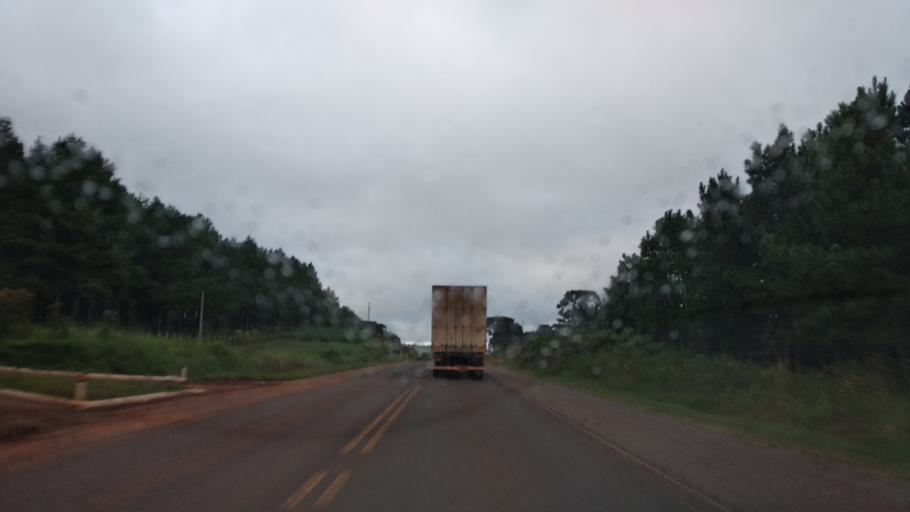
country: BR
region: Santa Catarina
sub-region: Campos Novos
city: Campos Novos
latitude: -27.4020
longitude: -51.0395
